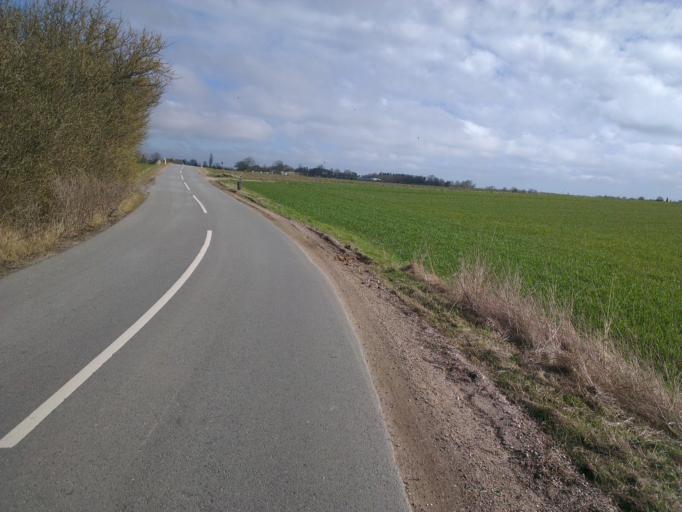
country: DK
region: Capital Region
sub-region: Frederikssund Kommune
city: Frederikssund
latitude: 55.8641
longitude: 12.1122
